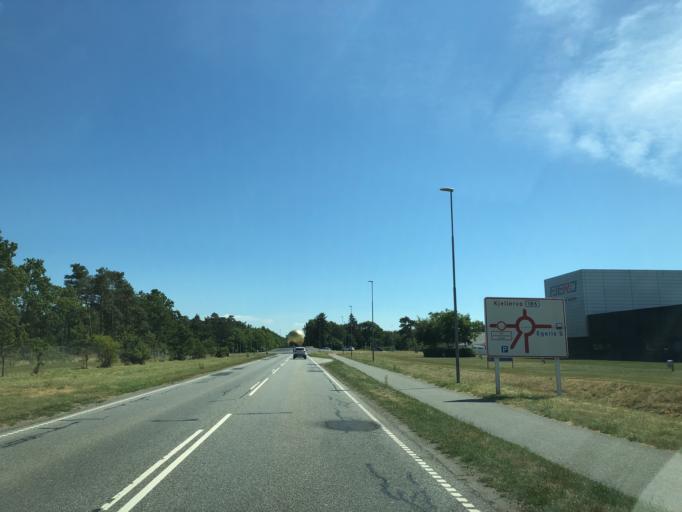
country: DK
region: Central Jutland
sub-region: Skive Kommune
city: Skive
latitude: 56.5377
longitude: 9.0365
